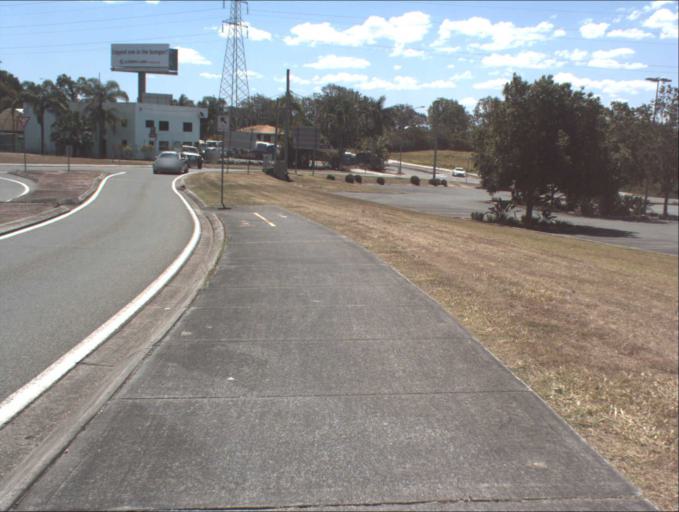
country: AU
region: Queensland
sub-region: Gold Coast
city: Yatala
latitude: -27.7227
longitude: 153.2185
